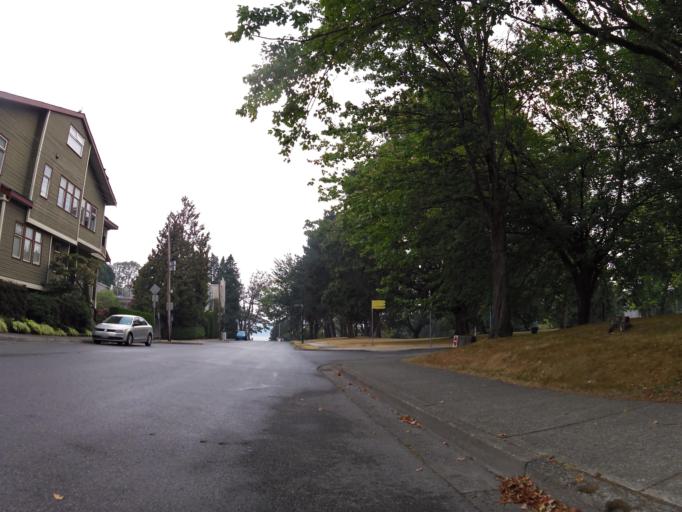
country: CA
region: British Columbia
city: West End
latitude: 49.2757
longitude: -123.1462
